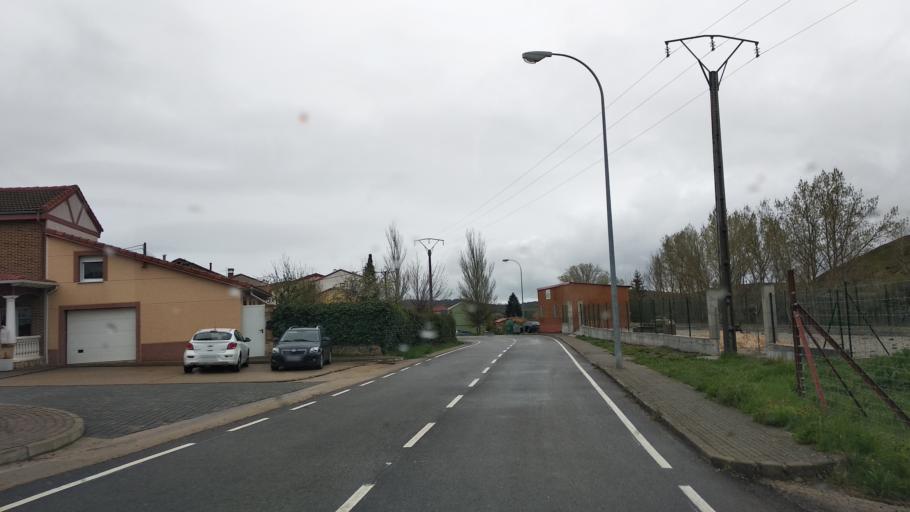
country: ES
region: Castille and Leon
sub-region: Provincia de Palencia
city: Barruelo de Santullan
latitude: 42.9015
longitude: -4.2874
